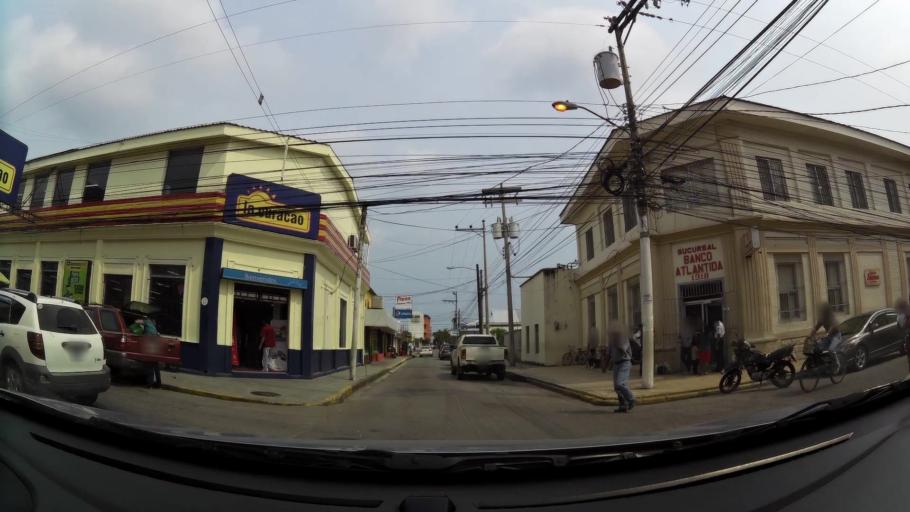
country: HN
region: Atlantida
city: Tela
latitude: 15.7826
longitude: -87.4520
